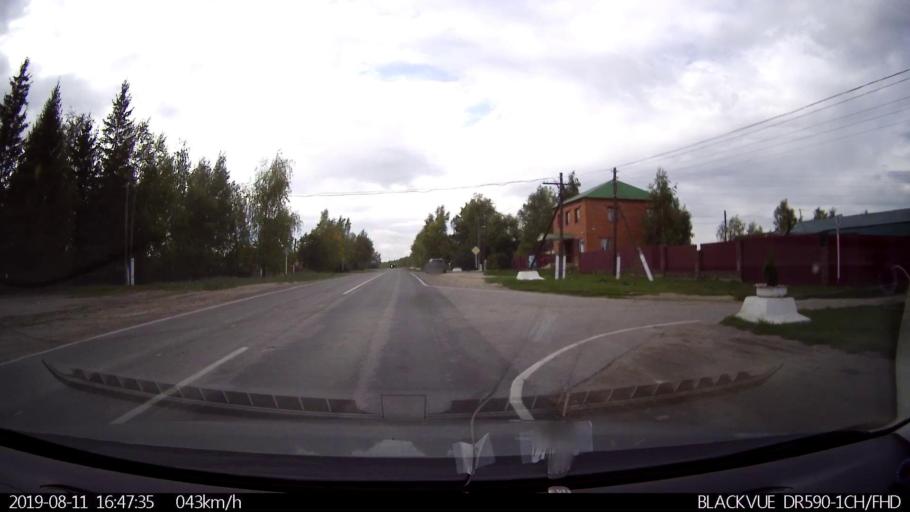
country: RU
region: Ulyanovsk
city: Mayna
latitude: 54.2038
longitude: 47.6950
